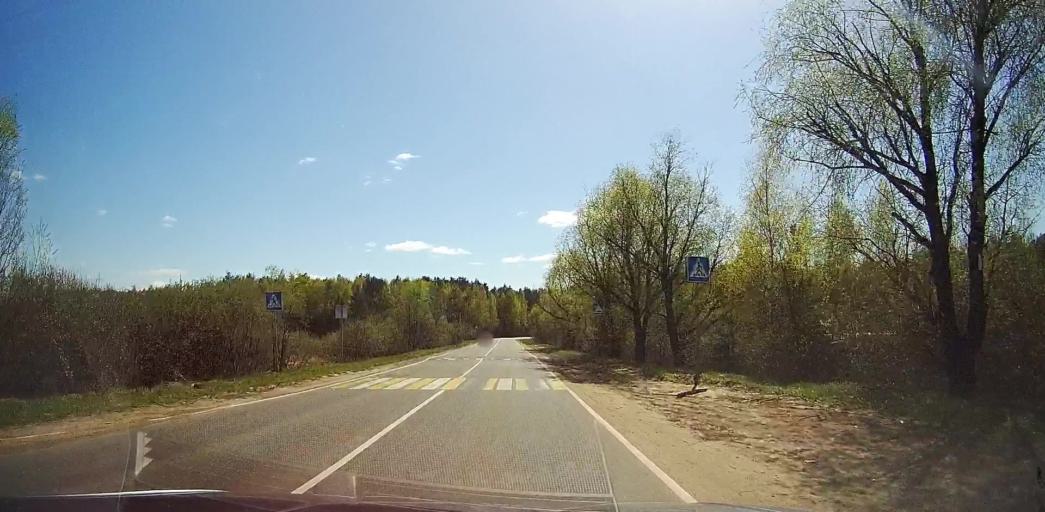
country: RU
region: Moskovskaya
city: Beloozerskiy
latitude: 55.5030
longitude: 38.4305
